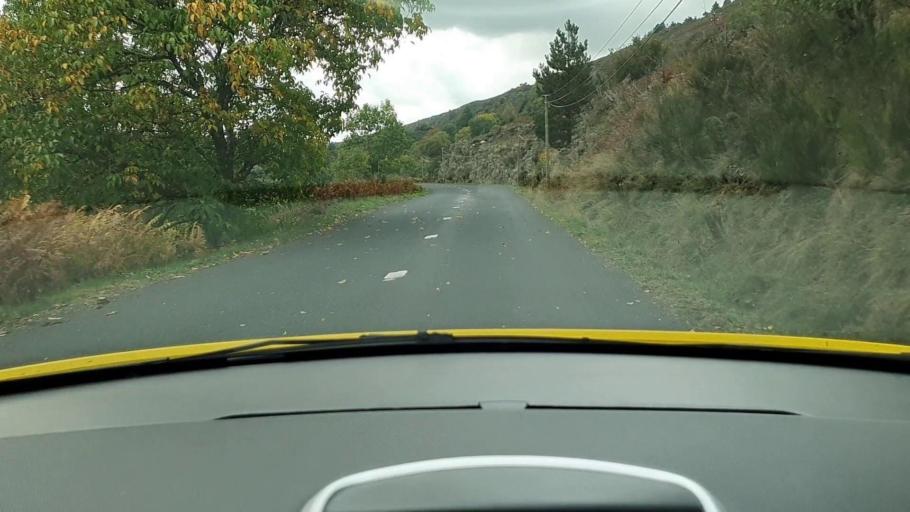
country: FR
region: Languedoc-Roussillon
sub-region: Departement de la Lozere
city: Meyrueis
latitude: 44.0808
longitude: 3.4691
